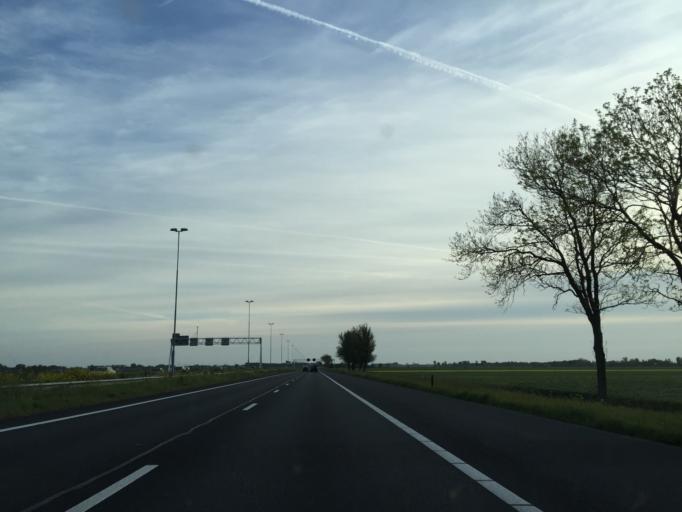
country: NL
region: North Holland
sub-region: Gemeente Beemster
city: Halfweg
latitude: 52.4912
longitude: 4.8884
